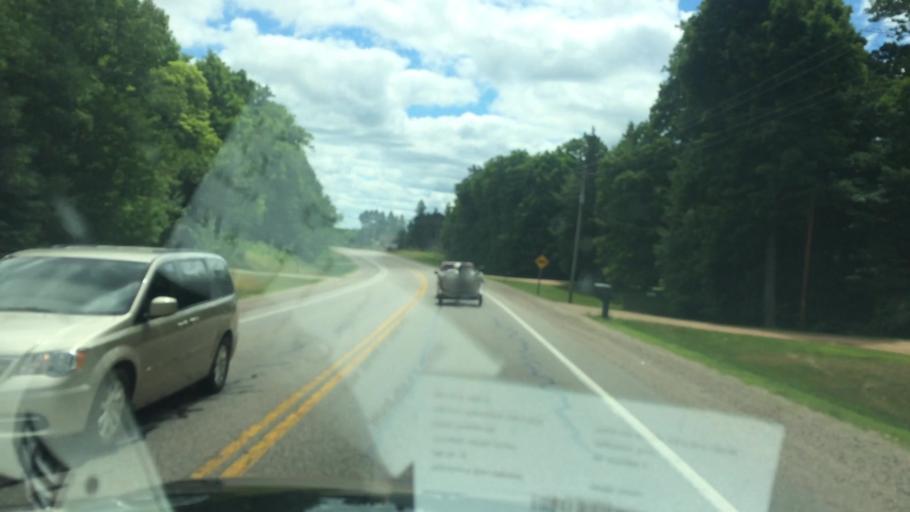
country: US
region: Wisconsin
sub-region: Vilas County
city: Eagle River
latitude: 45.7927
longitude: -89.3210
